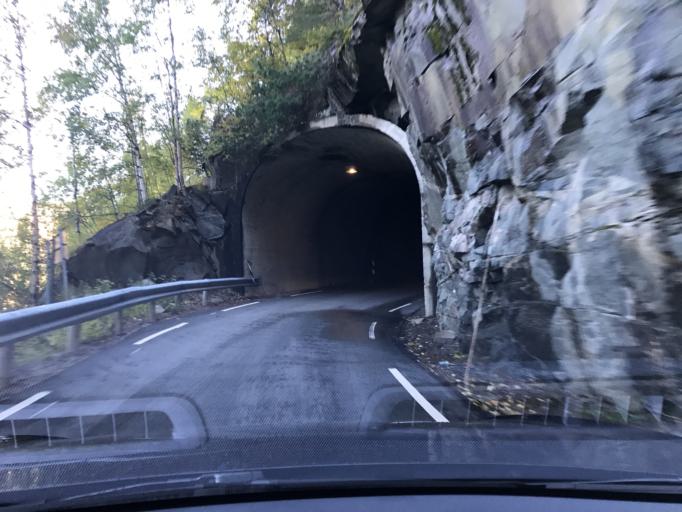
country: NO
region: Sogn og Fjordane
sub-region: Aurland
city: Aurlandsvangen
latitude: 60.8595
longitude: 7.3104
